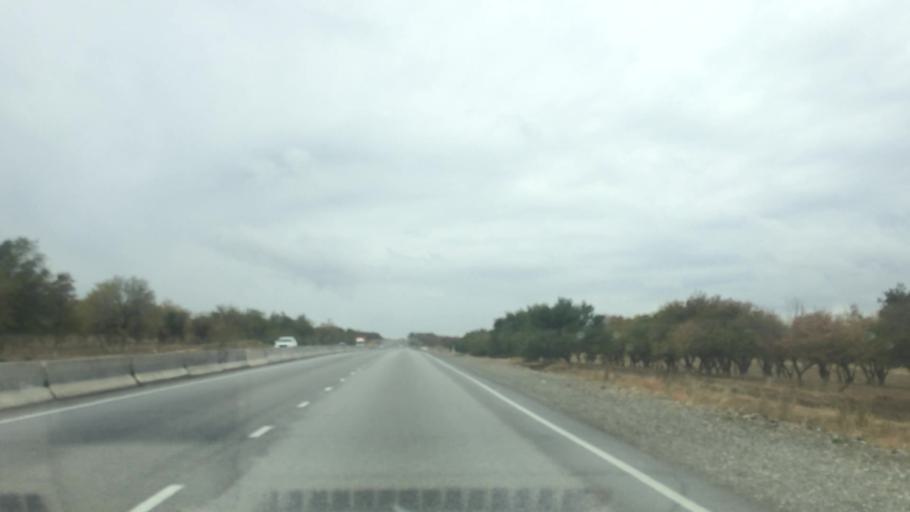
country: UZ
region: Samarqand
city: Bulung'ur
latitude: 39.8659
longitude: 67.4743
